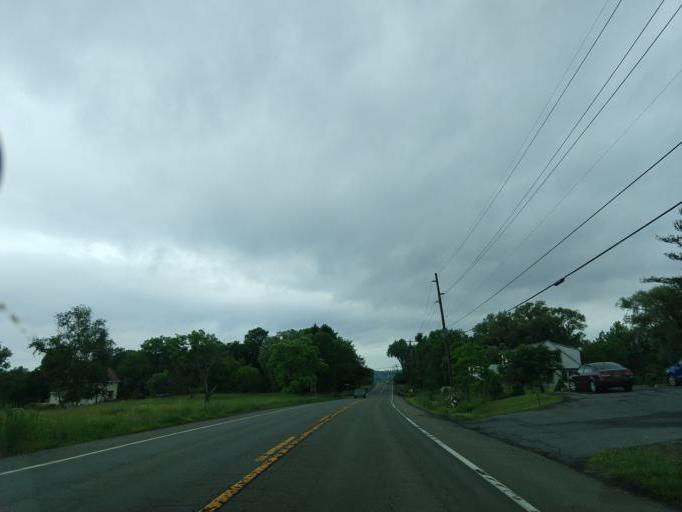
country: US
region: New York
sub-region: Tompkins County
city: Lansing
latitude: 42.5407
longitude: -76.5173
